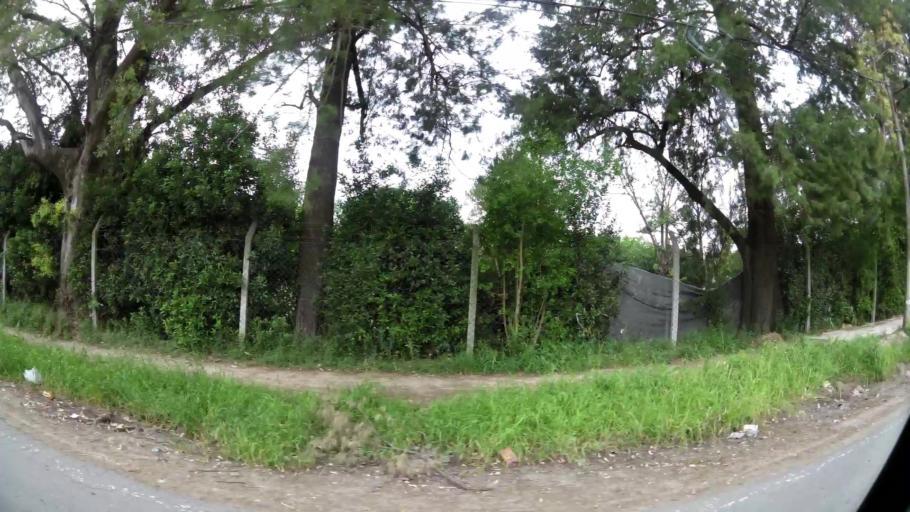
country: AR
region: Buenos Aires
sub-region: Partido de Ezeiza
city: Ezeiza
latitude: -34.8415
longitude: -58.5087
